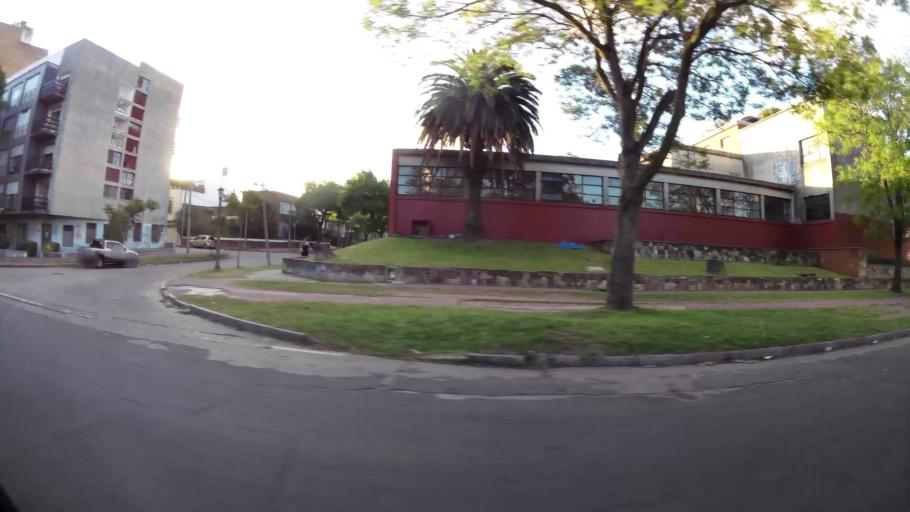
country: UY
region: Montevideo
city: Montevideo
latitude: -34.8883
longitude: -56.1541
